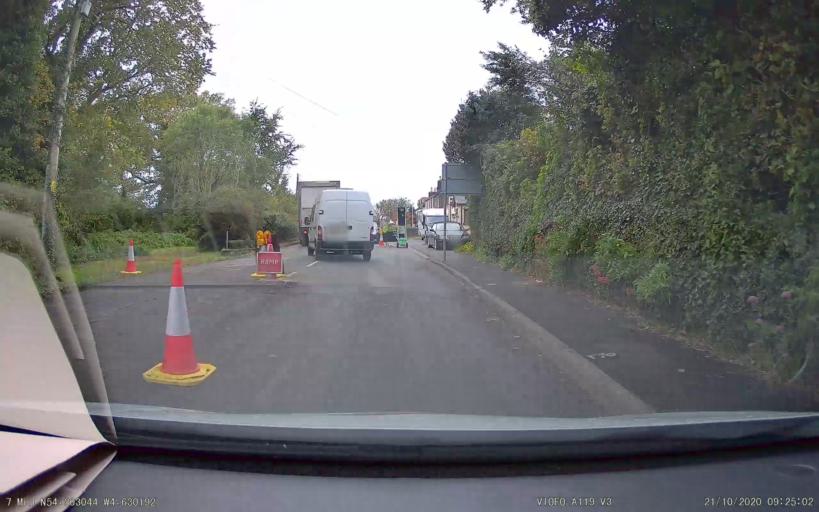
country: IM
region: Castletown
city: Castletown
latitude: 54.2030
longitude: -4.6302
